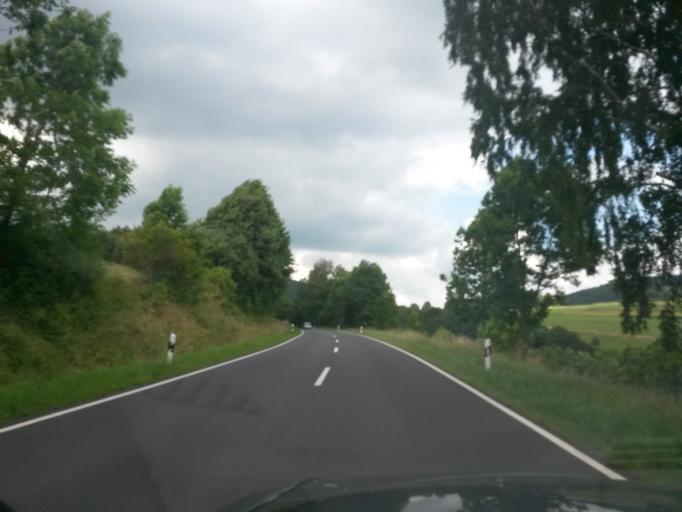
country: DE
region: Hesse
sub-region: Regierungsbezirk Kassel
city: Gersfeld
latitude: 50.4581
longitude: 9.9380
